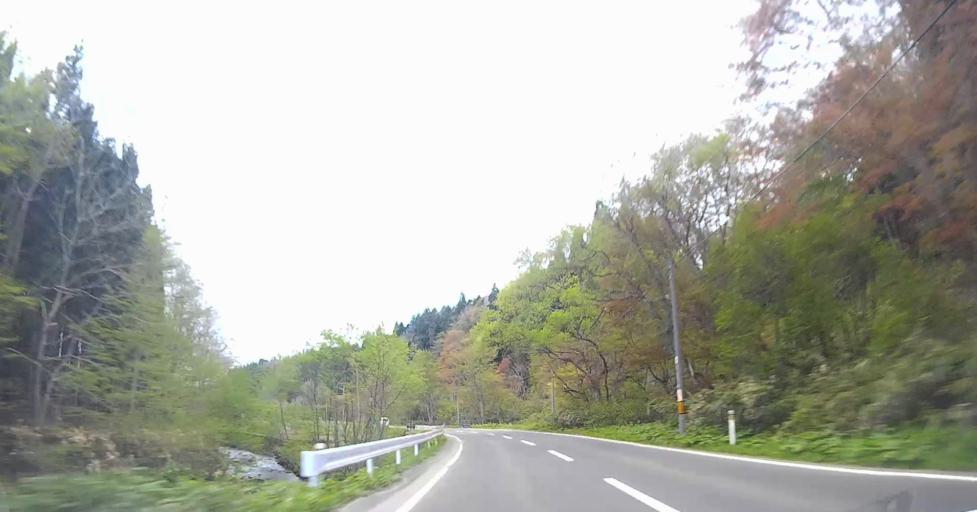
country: JP
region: Aomori
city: Goshogawara
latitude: 41.1260
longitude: 140.5195
